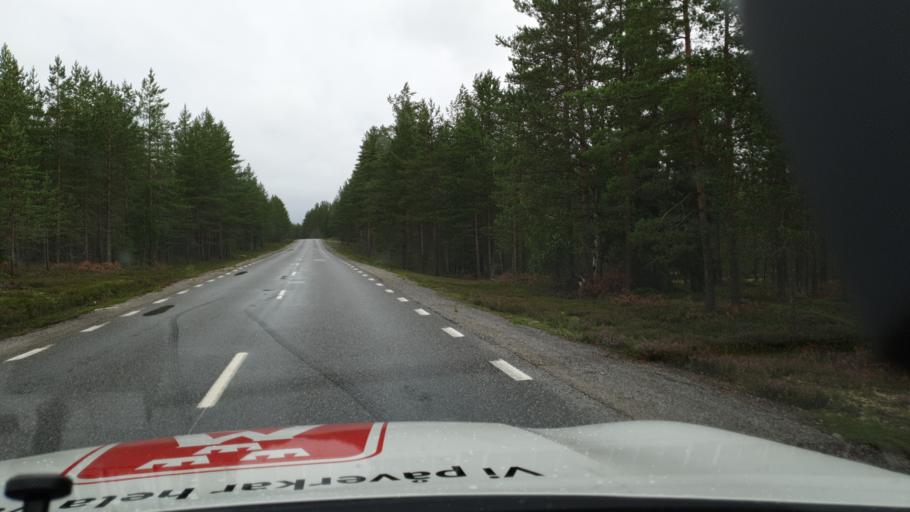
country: SE
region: Vaesterbotten
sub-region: Umea Kommun
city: Saevar
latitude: 64.0099
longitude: 20.4917
